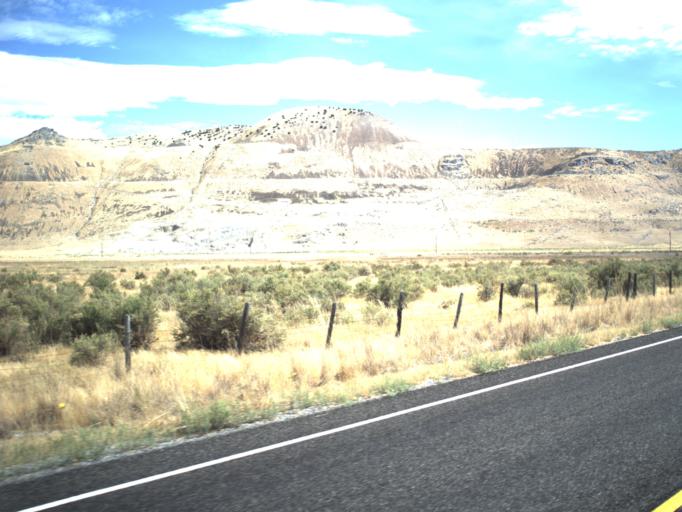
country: US
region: Utah
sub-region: Box Elder County
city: Tremonton
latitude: 41.5932
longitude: -112.2808
